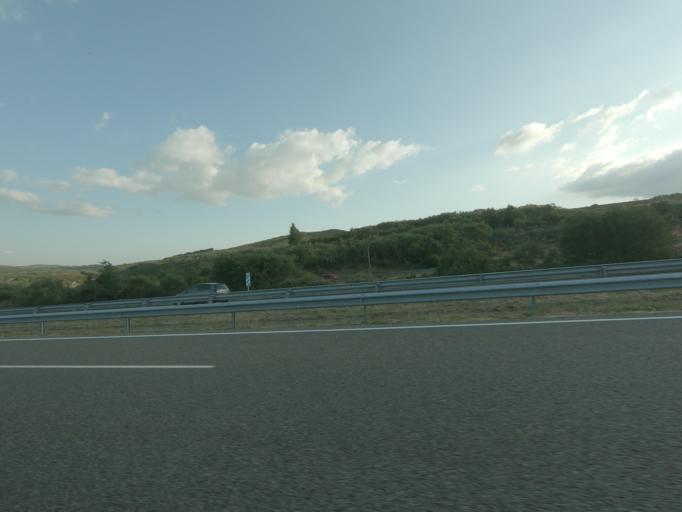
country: ES
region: Galicia
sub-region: Provincia de Ourense
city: Cualedro
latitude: 41.9872
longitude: -7.5507
